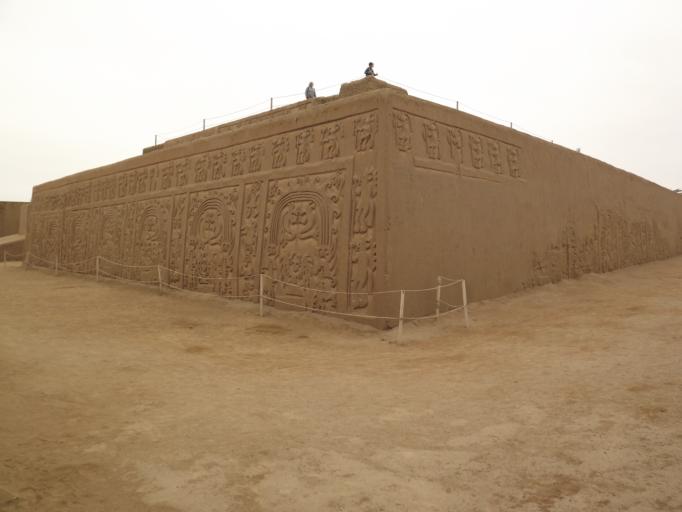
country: PE
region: La Libertad
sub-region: Provincia de Trujillo
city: La Esperanza
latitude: -8.0767
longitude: -79.0488
